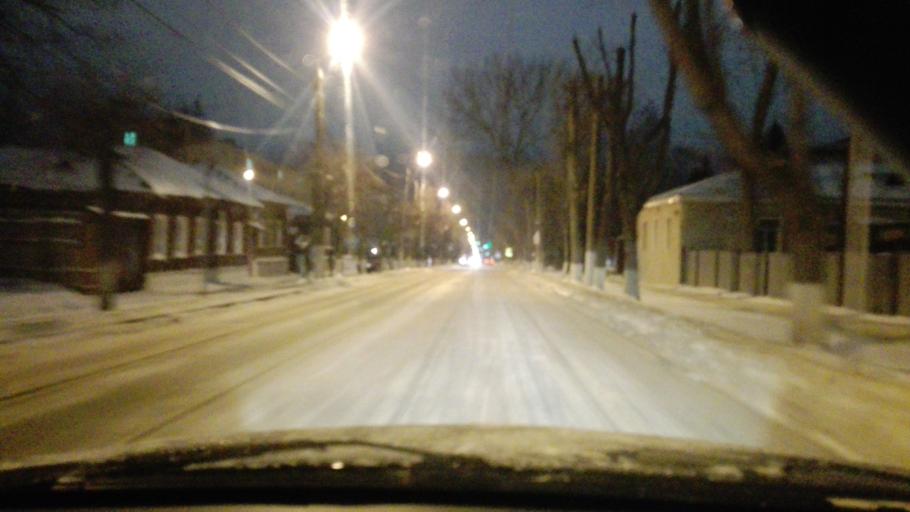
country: RU
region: Tula
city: Tula
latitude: 54.1847
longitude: 37.6044
